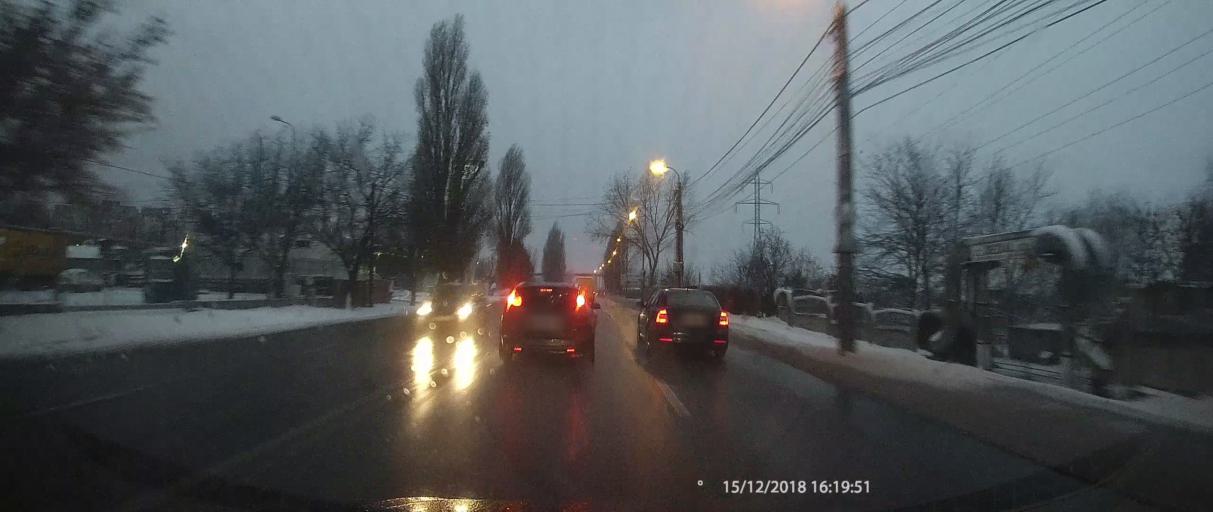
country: RO
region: Galati
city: Galati
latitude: 45.4173
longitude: 28.0049
